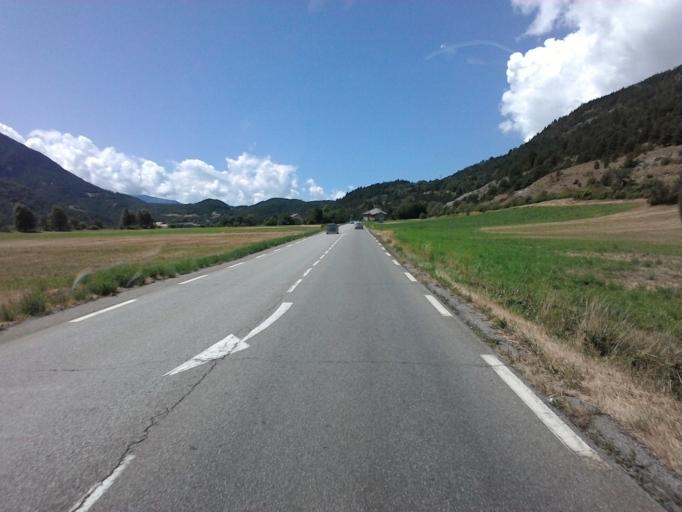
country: FR
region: Provence-Alpes-Cote d'Azur
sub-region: Departement des Hautes-Alpes
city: Guillestre
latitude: 44.6436
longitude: 6.5730
